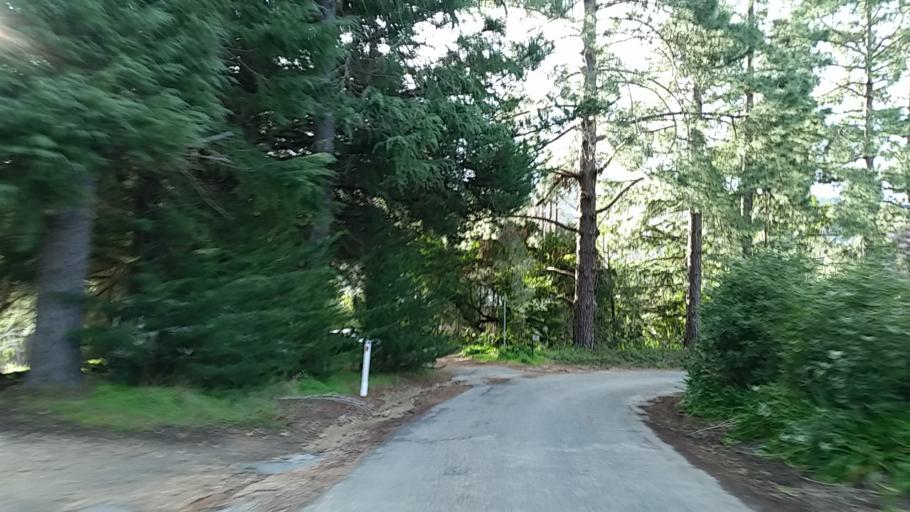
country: AU
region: South Australia
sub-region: Adelaide Hills
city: Adelaide Hills
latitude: -34.9360
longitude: 138.7664
